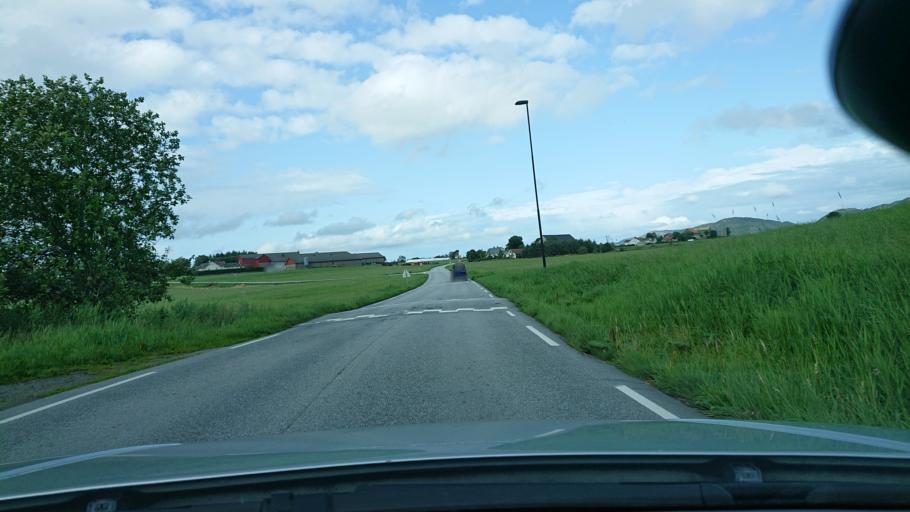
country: NO
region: Rogaland
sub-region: Gjesdal
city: Algard
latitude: 58.6885
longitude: 5.7682
